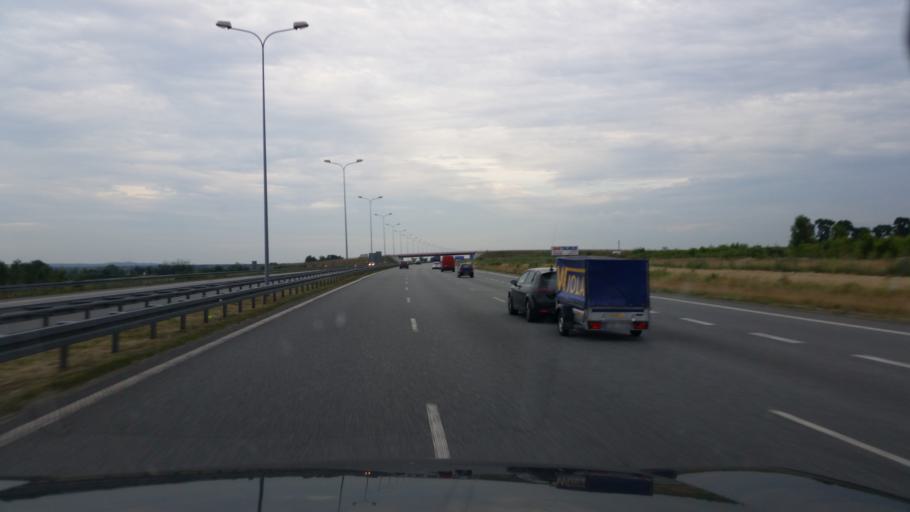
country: PL
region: Silesian Voivodeship
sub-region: Powiat gliwicki
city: Gieraltowice
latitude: 50.2465
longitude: 18.7136
